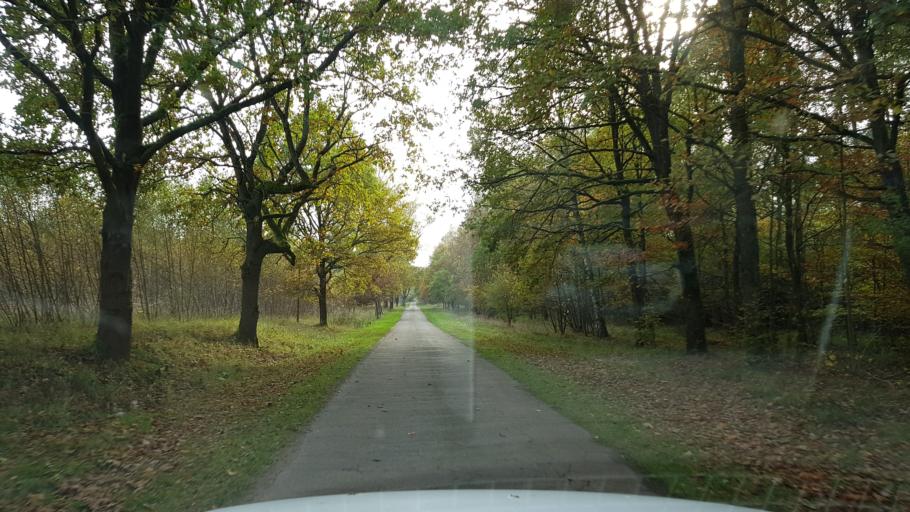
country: PL
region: West Pomeranian Voivodeship
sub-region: Powiat lobeski
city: Wegorzyno
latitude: 53.5131
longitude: 15.4965
